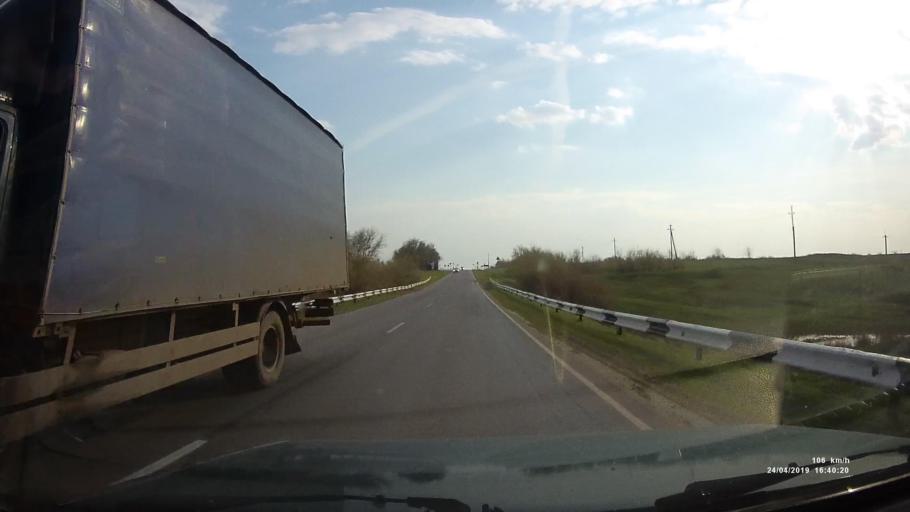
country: RU
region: Rostov
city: Gundorovskiy
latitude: 46.8343
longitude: 41.8832
